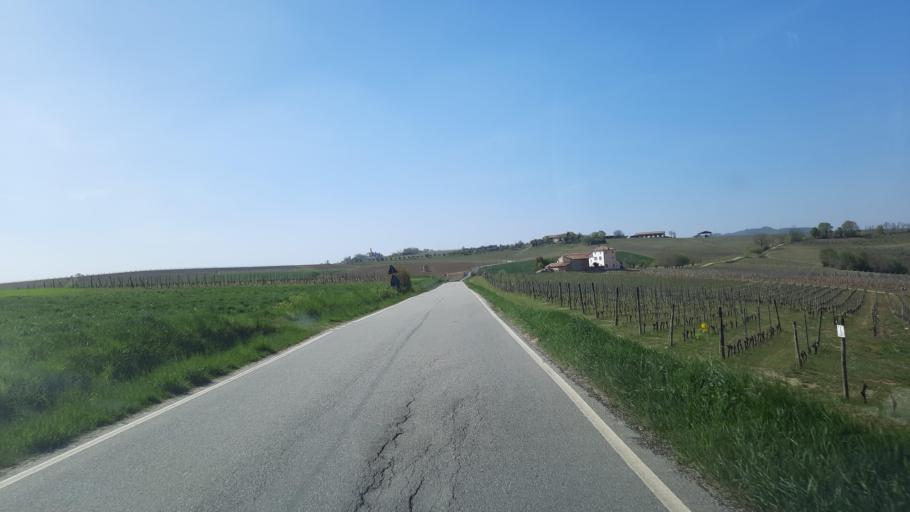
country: IT
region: Piedmont
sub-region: Provincia di Alessandria
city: Olivola
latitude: 45.0169
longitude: 8.3624
